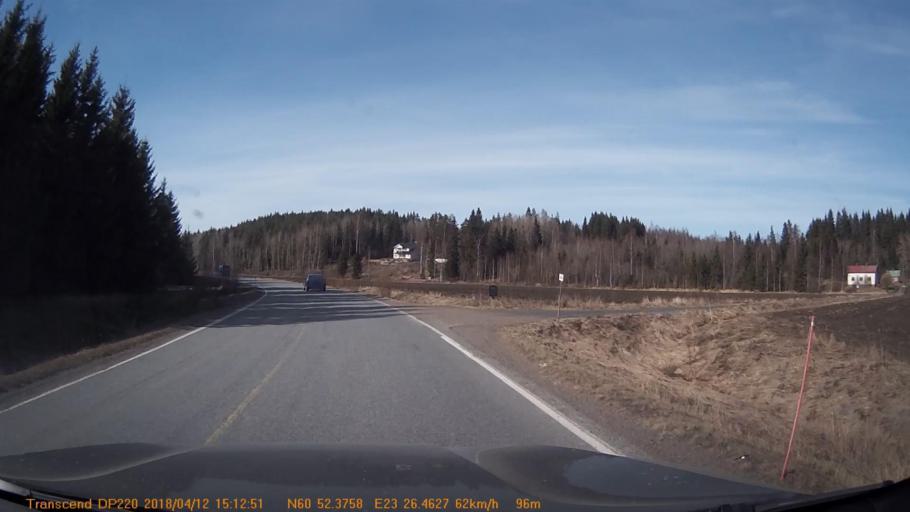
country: FI
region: Haeme
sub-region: Forssa
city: Jokioinen
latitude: 60.8729
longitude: 23.4411
